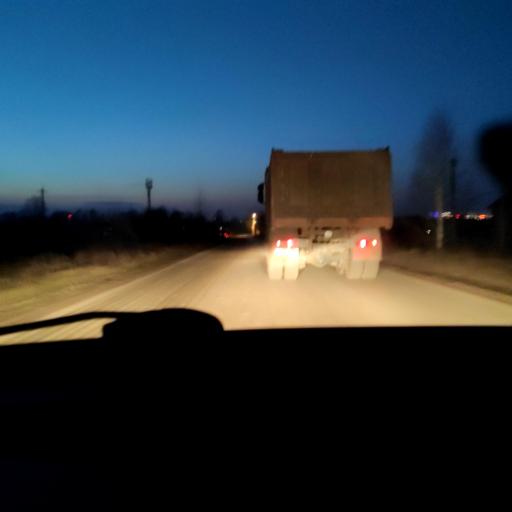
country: RU
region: Bashkortostan
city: Ufa
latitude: 54.7059
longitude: 56.1094
